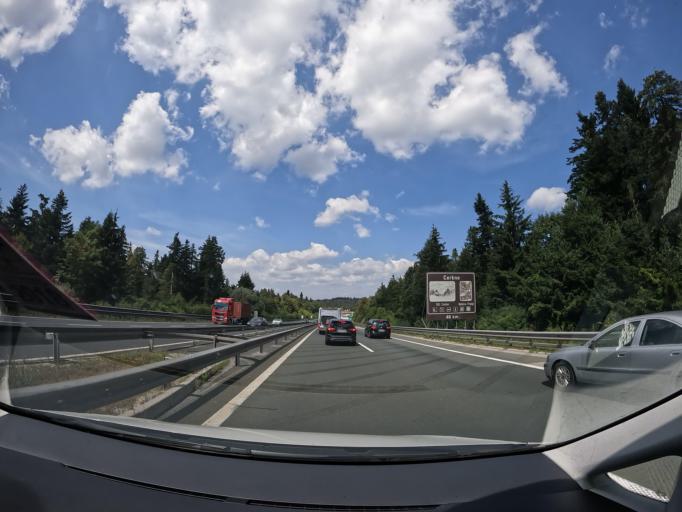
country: SI
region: Logatec
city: Logatec
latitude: 45.8928
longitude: 14.2570
